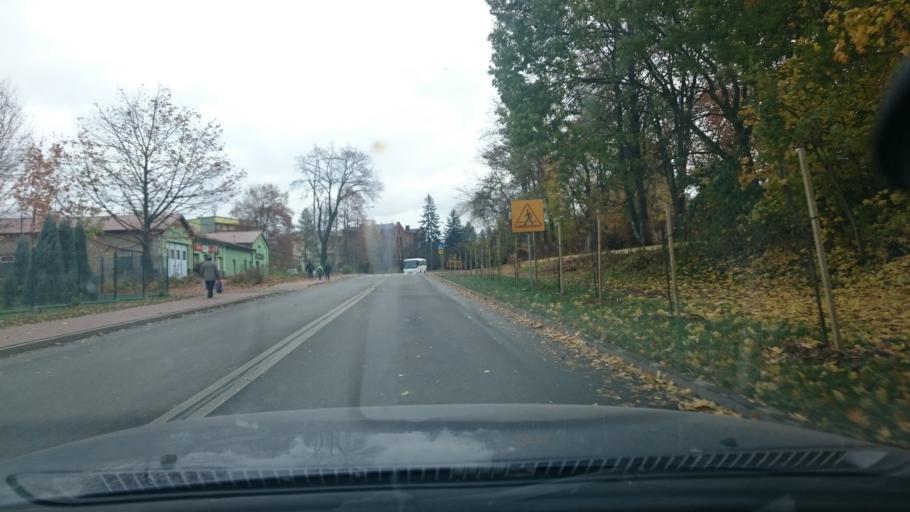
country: PL
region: Silesian Voivodeship
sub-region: Powiat bedzinski
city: Strzyzowice
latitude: 50.3533
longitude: 19.0758
